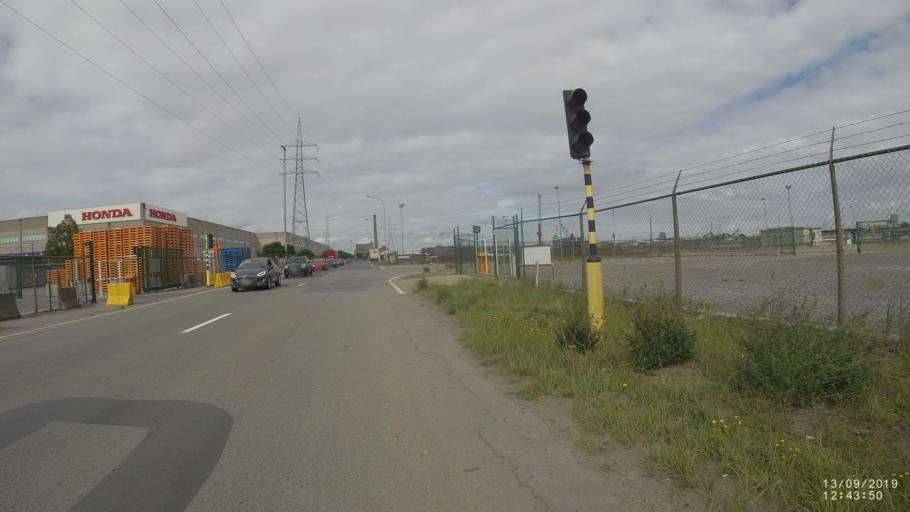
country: BE
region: Flanders
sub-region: Provincie Oost-Vlaanderen
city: Evergem
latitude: 51.1082
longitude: 3.7580
